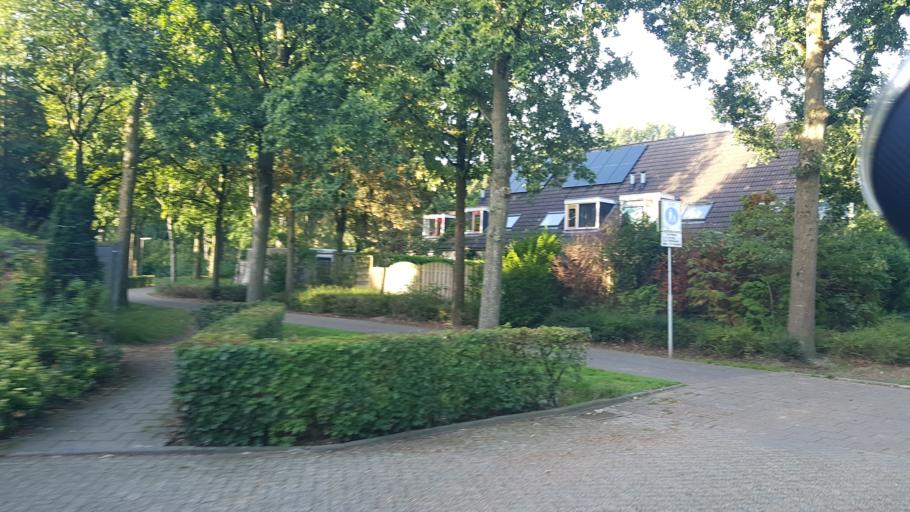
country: NL
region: Gelderland
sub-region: Gemeente Apeldoorn
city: Apeldoorn
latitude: 52.2007
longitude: 5.9971
